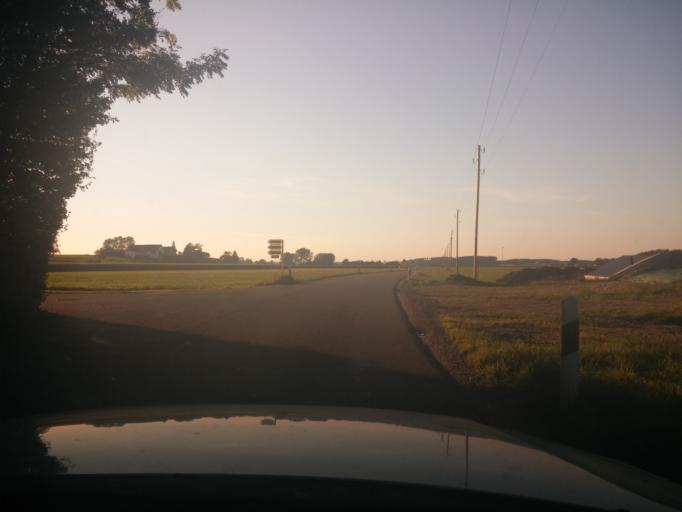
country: DE
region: Bavaria
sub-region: Swabia
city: Altusried
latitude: 47.8288
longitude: 10.1752
